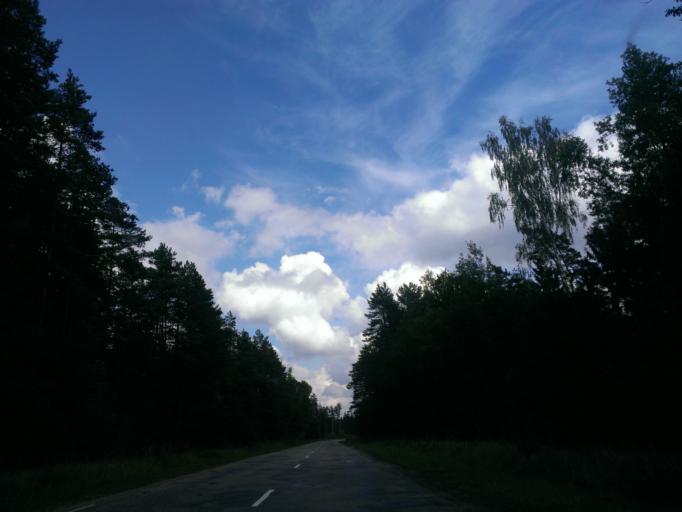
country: LV
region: Ropazu
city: Ropazi
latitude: 57.0234
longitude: 24.6279
